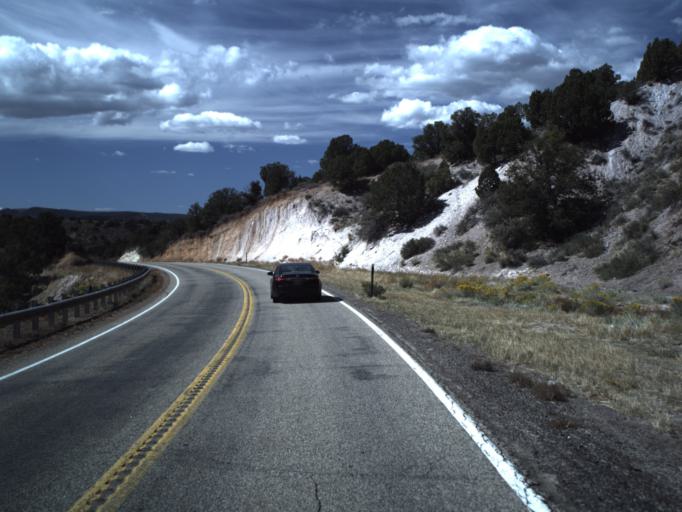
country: US
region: Utah
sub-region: Washington County
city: Enterprise
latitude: 37.5408
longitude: -113.6751
